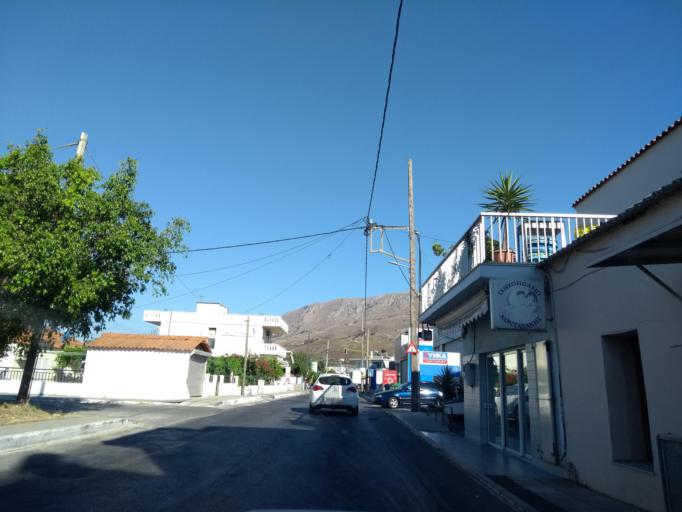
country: GR
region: Crete
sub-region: Nomos Chanias
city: Souda
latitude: 35.4899
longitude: 24.0628
